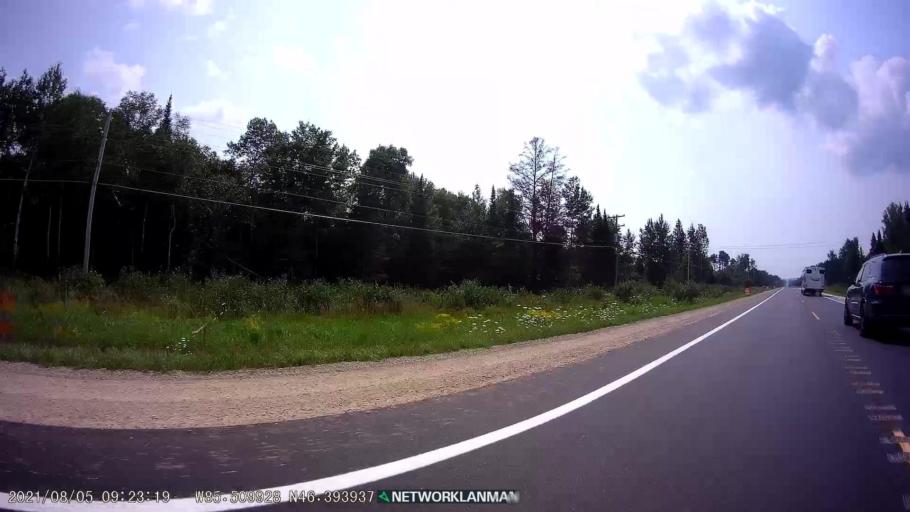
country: US
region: Michigan
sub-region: Luce County
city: Newberry
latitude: 46.3934
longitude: -85.5099
